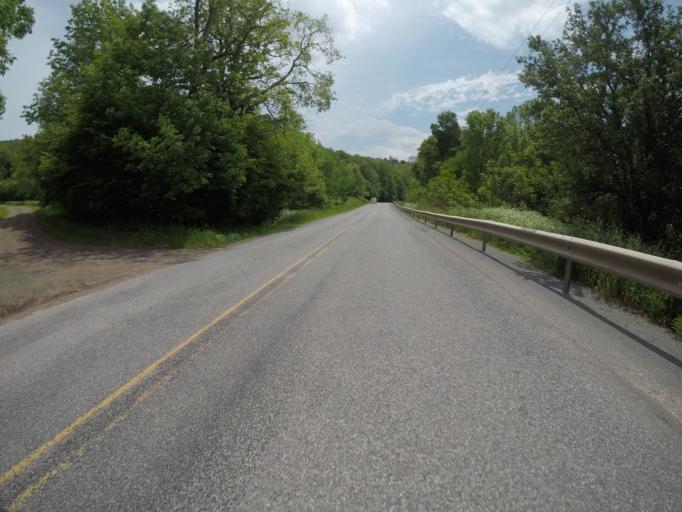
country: US
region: New York
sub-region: Delaware County
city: Stamford
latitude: 42.1857
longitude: -74.6715
